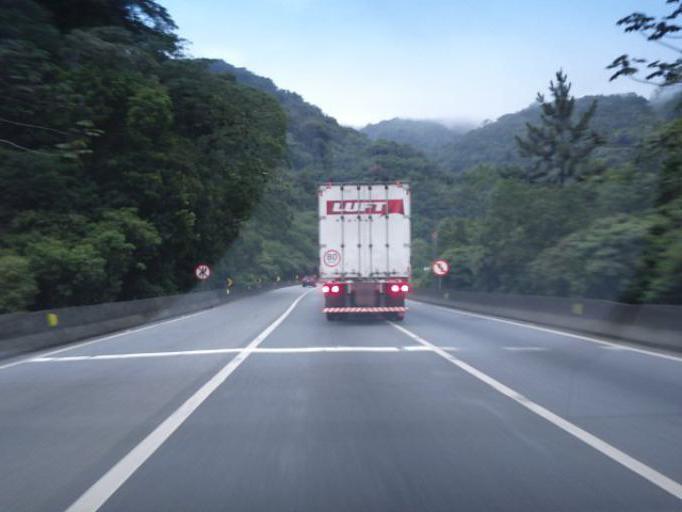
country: BR
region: Parana
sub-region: Guaratuba
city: Guaratuba
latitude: -25.8643
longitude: -48.9378
